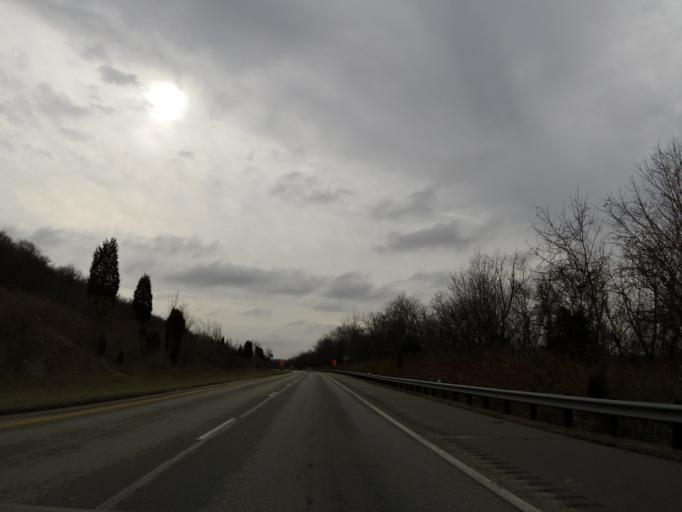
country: US
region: Ohio
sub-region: Hamilton County
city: Cleves
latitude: 39.2008
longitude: -84.7670
